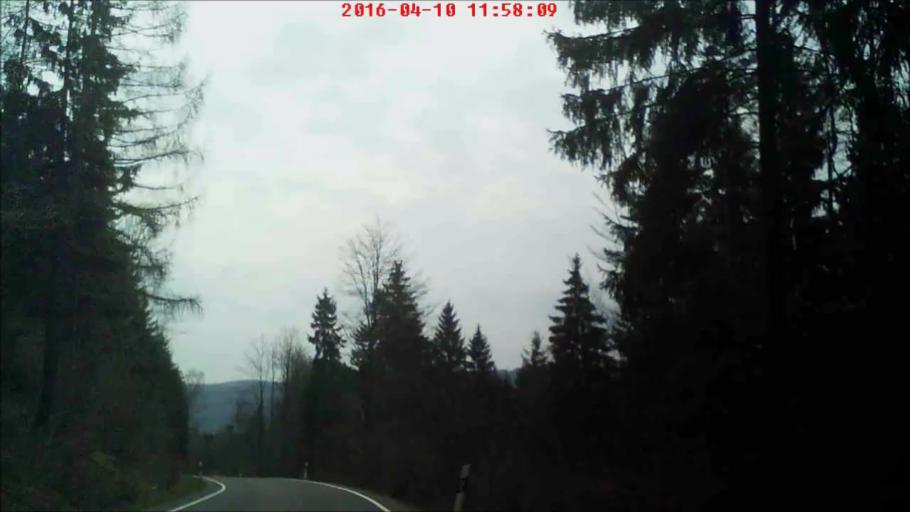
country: DE
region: Thuringia
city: Zella-Mehlis
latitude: 50.6765
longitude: 10.6491
